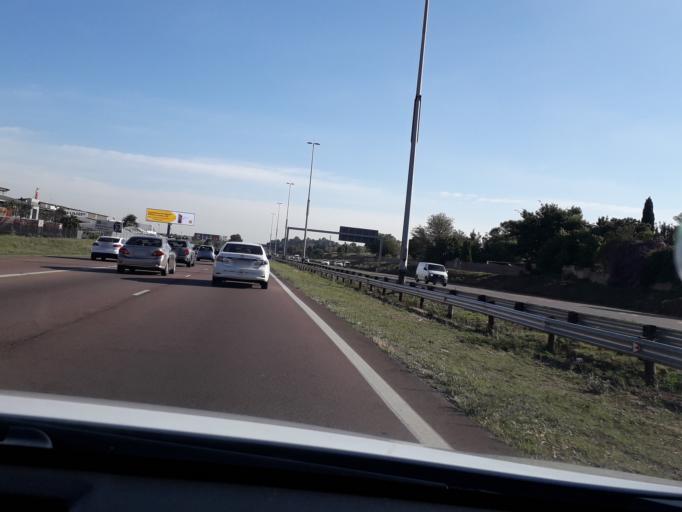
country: ZA
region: Gauteng
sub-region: City of Tshwane Metropolitan Municipality
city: Centurion
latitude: -25.8713
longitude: 28.1703
